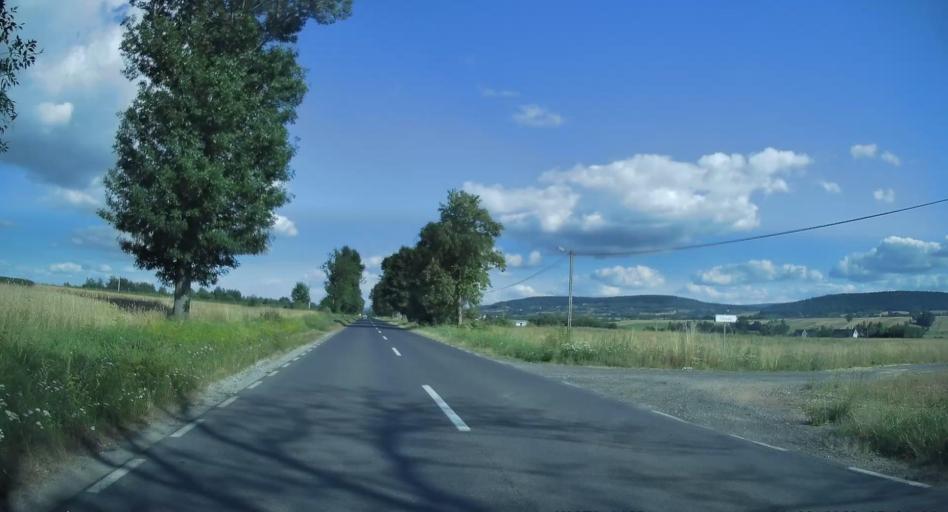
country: PL
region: Swietokrzyskie
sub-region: Powiat kielecki
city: Bodzentyn
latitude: 50.9582
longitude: 20.9101
